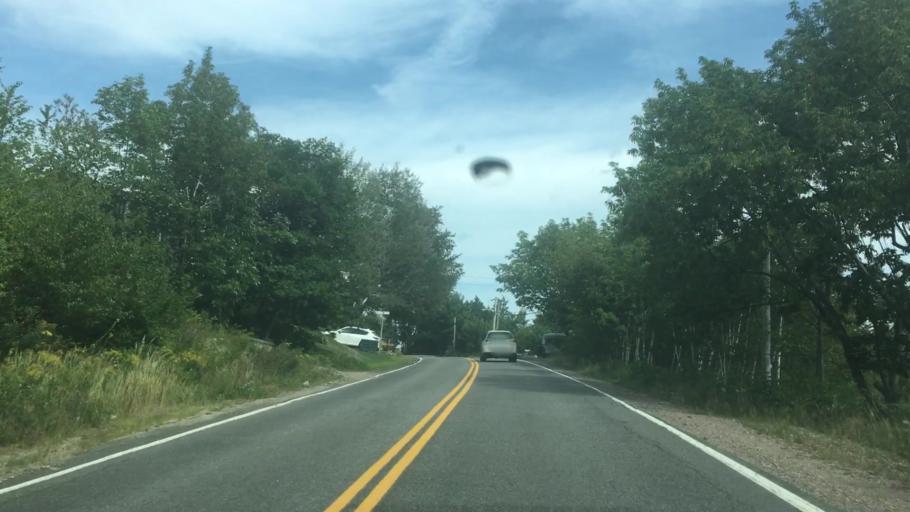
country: CA
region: Nova Scotia
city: Sydney Mines
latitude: 46.6356
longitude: -60.4151
